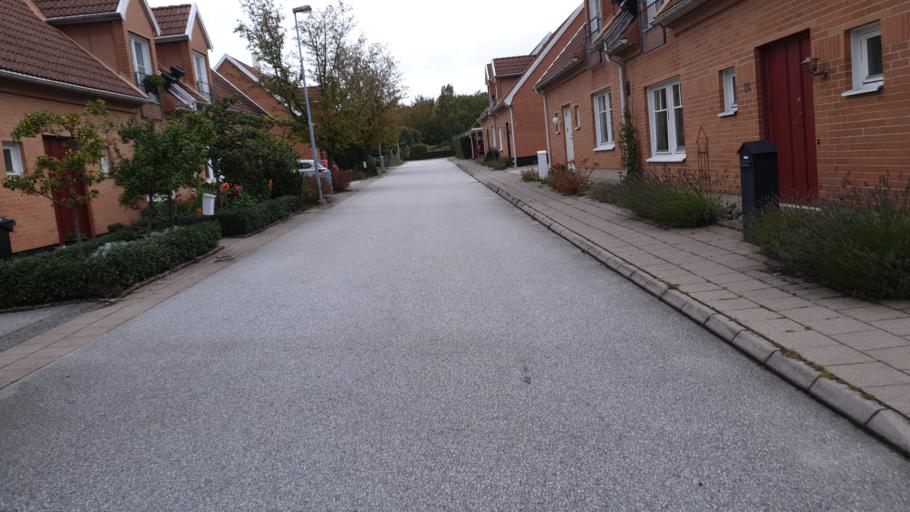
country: SE
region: Skane
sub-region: Lunds Kommun
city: Lund
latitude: 55.7161
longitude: 13.2387
